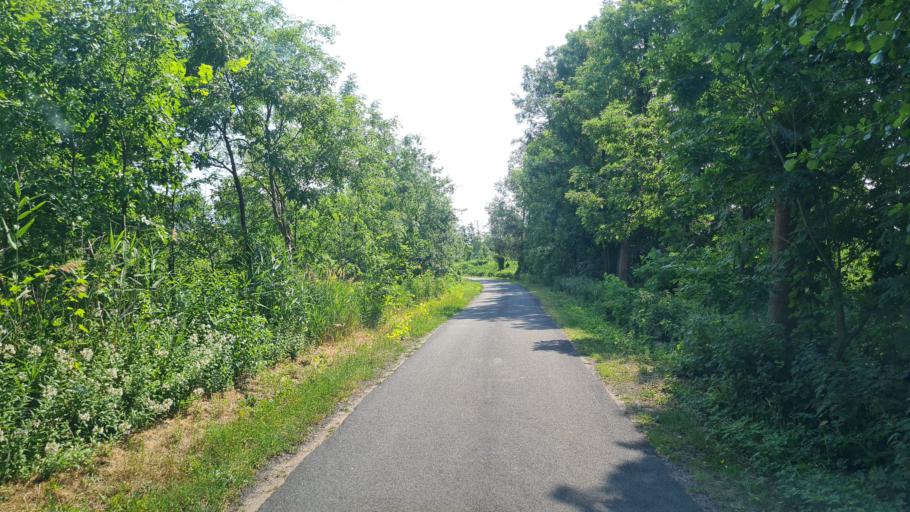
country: DE
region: Brandenburg
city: Wollin
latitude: 52.3245
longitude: 12.5365
